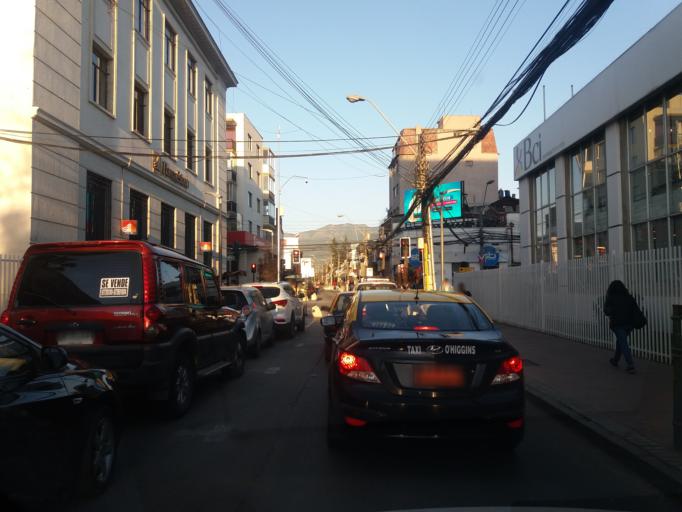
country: CL
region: Valparaiso
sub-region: Provincia de Quillota
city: Quillota
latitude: -32.8783
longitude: -71.2470
